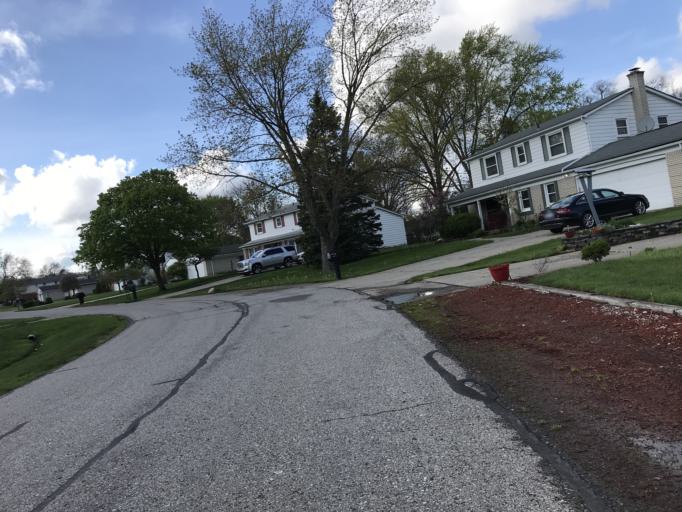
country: US
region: Michigan
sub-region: Oakland County
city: Farmington Hills
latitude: 42.4809
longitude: -83.3349
